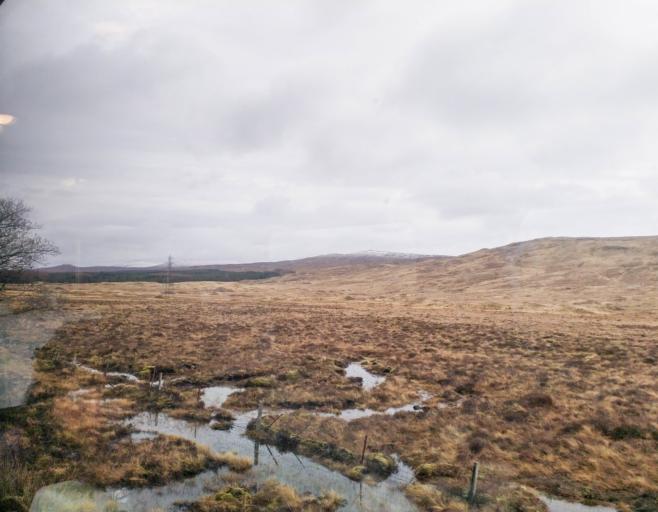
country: GB
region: Scotland
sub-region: Highland
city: Spean Bridge
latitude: 56.5976
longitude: -4.6126
